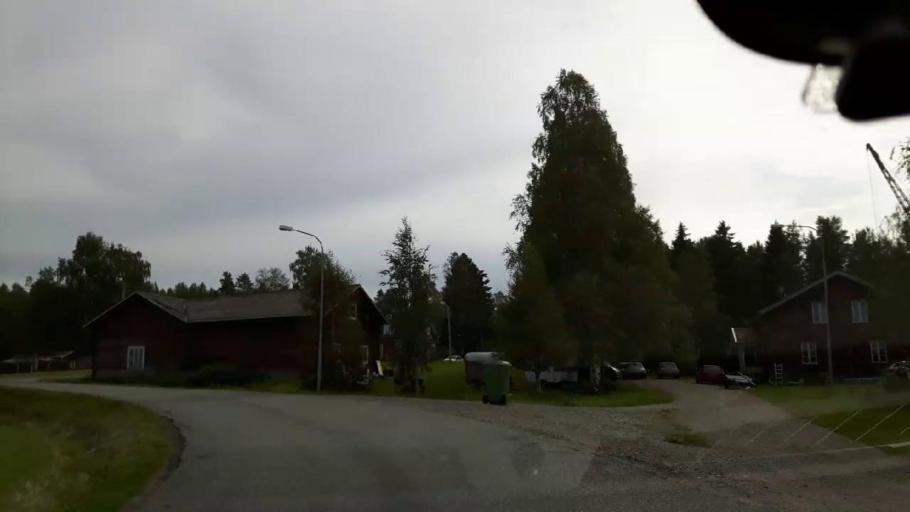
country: SE
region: Jaemtland
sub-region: Ragunda Kommun
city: Hammarstrand
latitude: 63.0072
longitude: 16.0867
